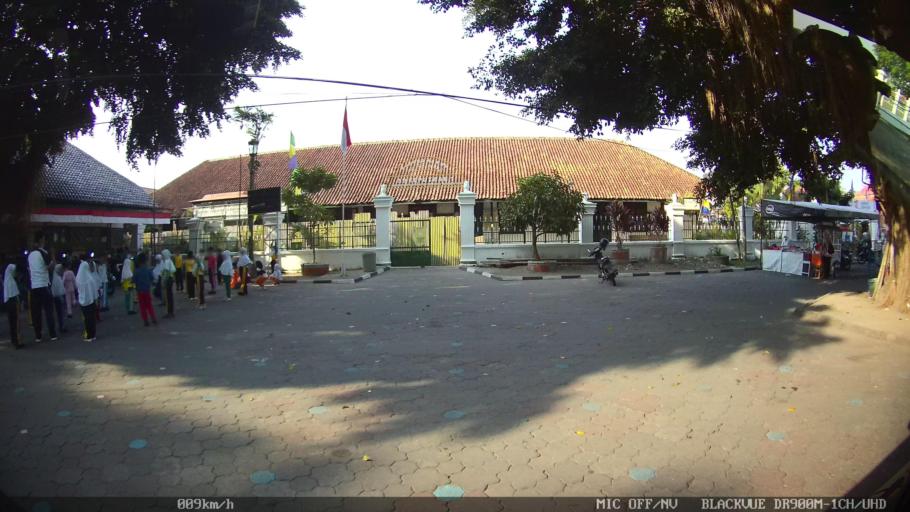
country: ID
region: Daerah Istimewa Yogyakarta
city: Yogyakarta
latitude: -7.8051
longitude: 110.3650
